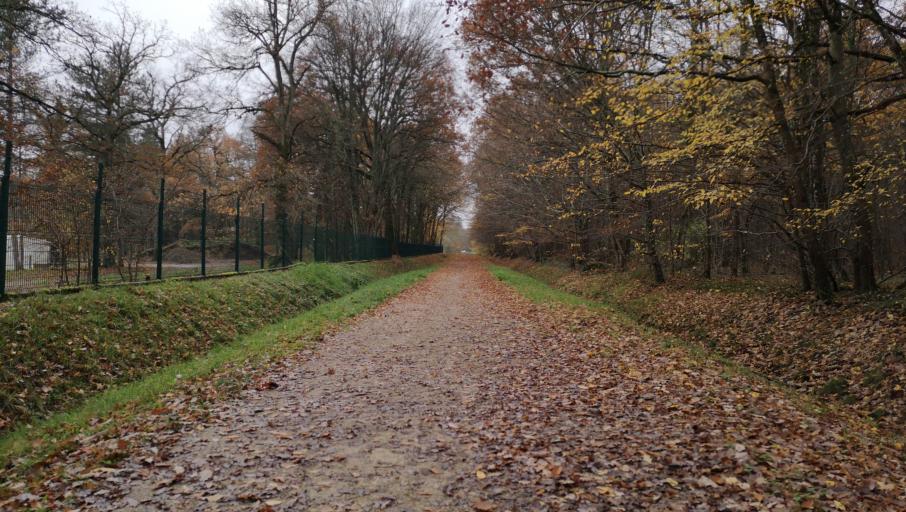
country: FR
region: Centre
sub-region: Departement du Loiret
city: Saint-Jean-de-Braye
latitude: 47.9278
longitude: 1.9861
